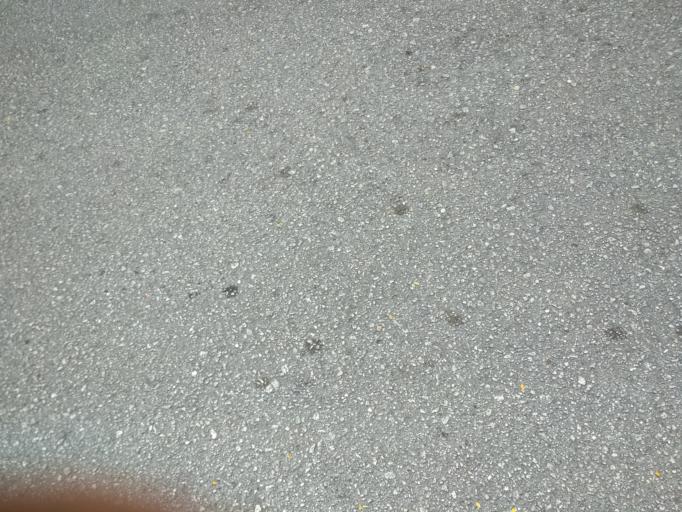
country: MY
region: Perak
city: Ipoh
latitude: 4.6060
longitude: 101.1187
